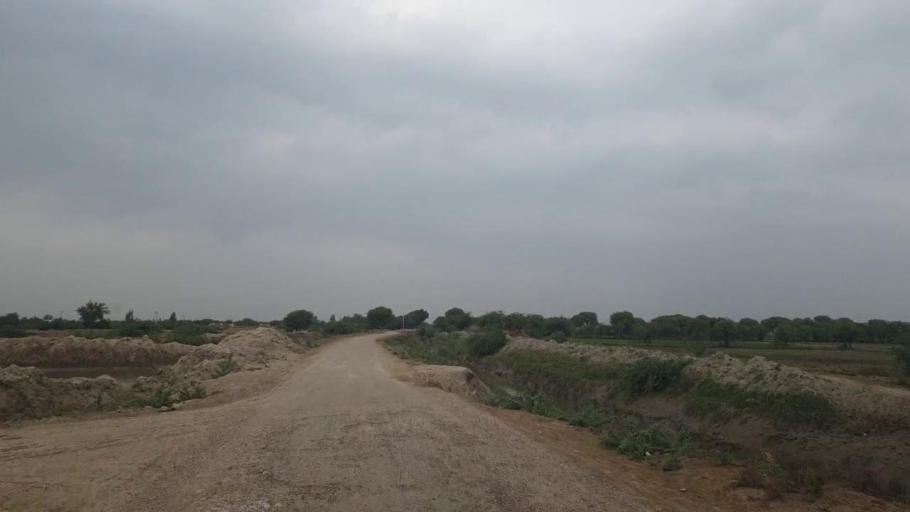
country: PK
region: Sindh
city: Badin
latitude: 24.6293
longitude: 68.6817
